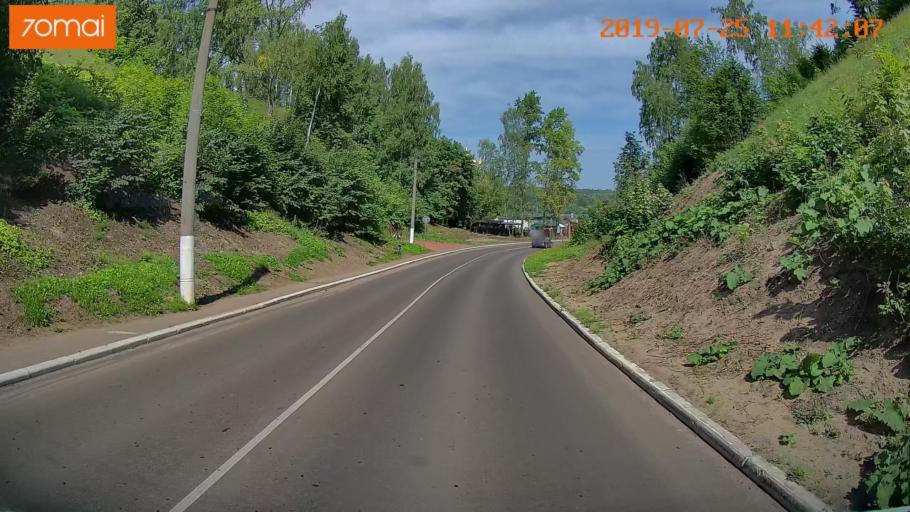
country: RU
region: Ivanovo
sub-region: Privolzhskiy Rayon
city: Ples
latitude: 57.4589
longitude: 41.5118
